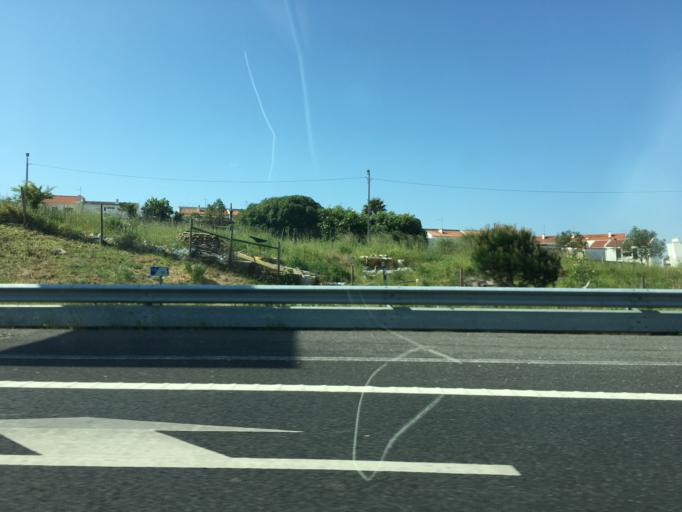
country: PT
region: Lisbon
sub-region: Sintra
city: Cacem
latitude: 38.7891
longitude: -9.3025
